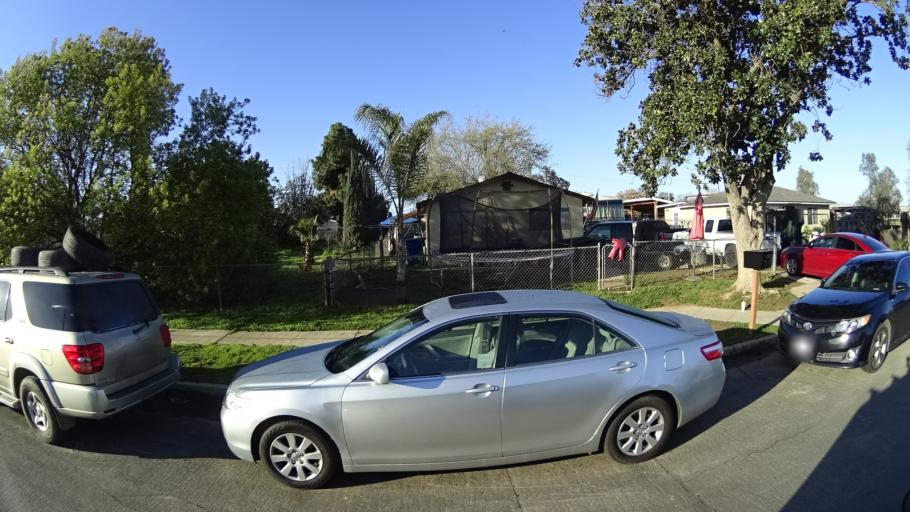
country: US
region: California
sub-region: Fresno County
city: Biola
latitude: 36.8386
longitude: -119.9191
